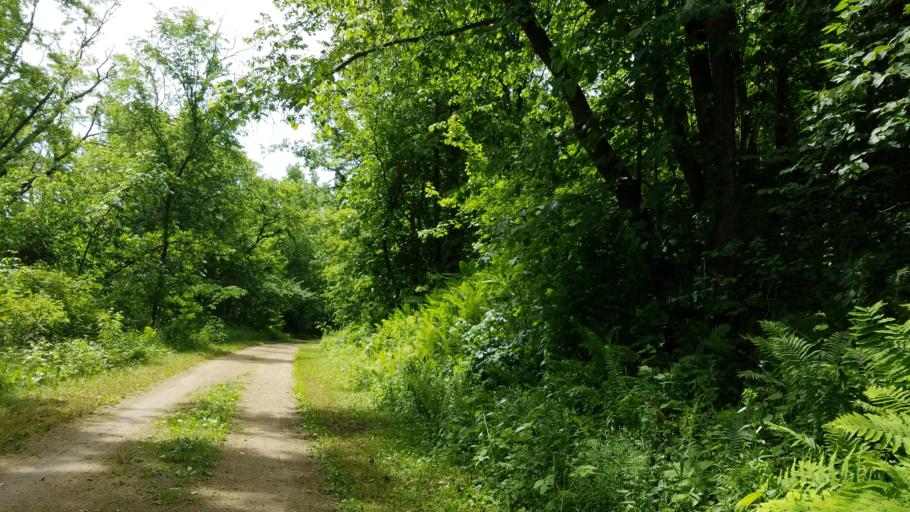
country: US
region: Wisconsin
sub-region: Dunn County
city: Menomonie
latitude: 44.8084
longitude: -91.9479
